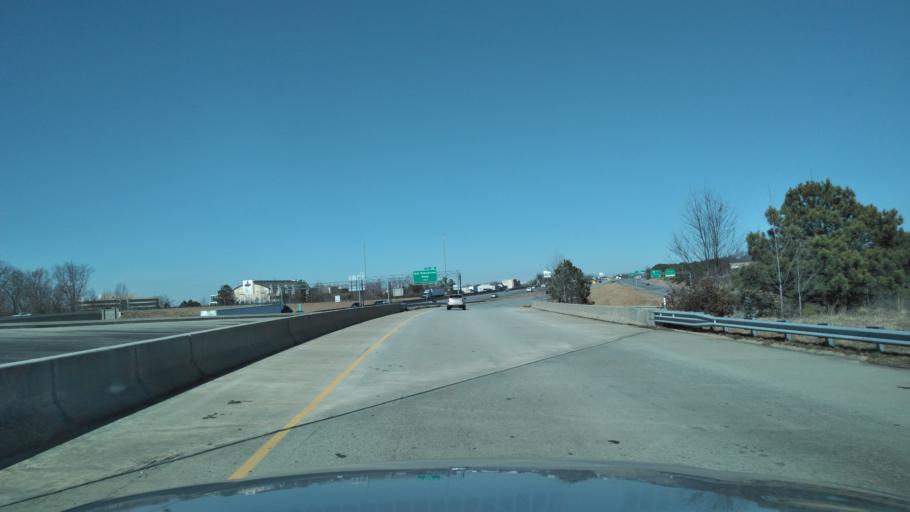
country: US
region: Georgia
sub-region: Gwinnett County
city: Duluth
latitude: 33.9804
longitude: -84.0868
